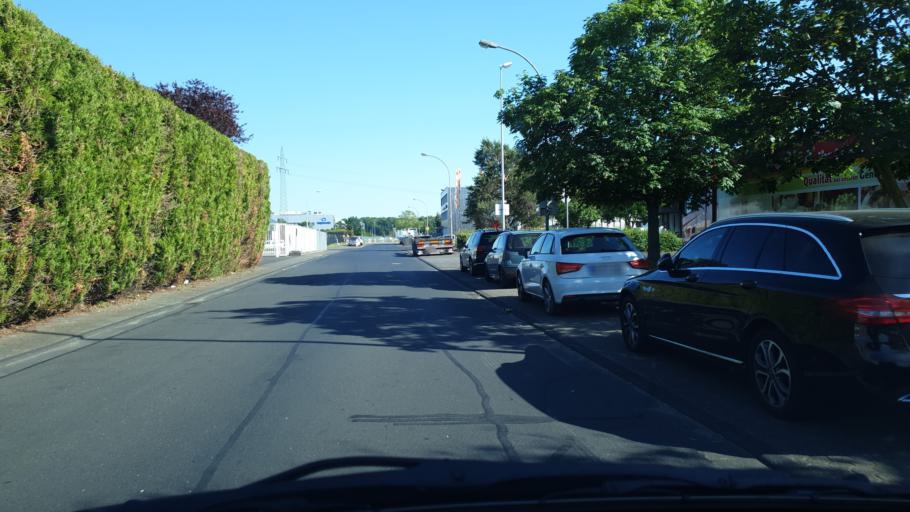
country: DE
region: North Rhine-Westphalia
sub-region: Regierungsbezirk Koln
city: Kerpen
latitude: 50.8960
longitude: 6.6656
